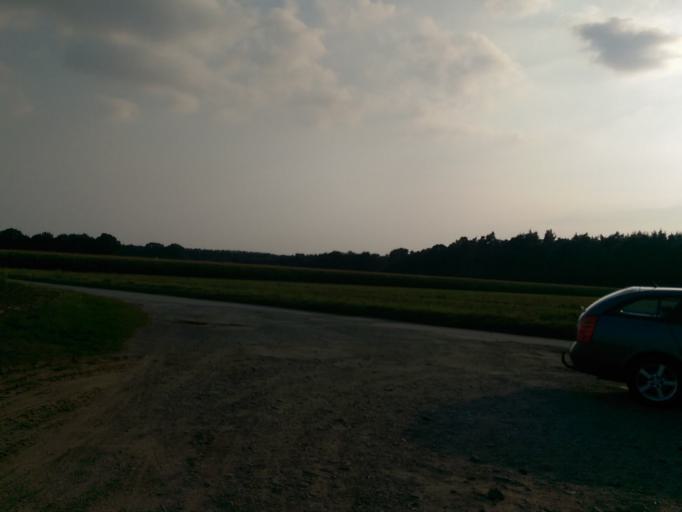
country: DE
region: North Rhine-Westphalia
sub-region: Regierungsbezirk Detmold
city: Rheda-Wiedenbruck
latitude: 51.8893
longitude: 8.3249
